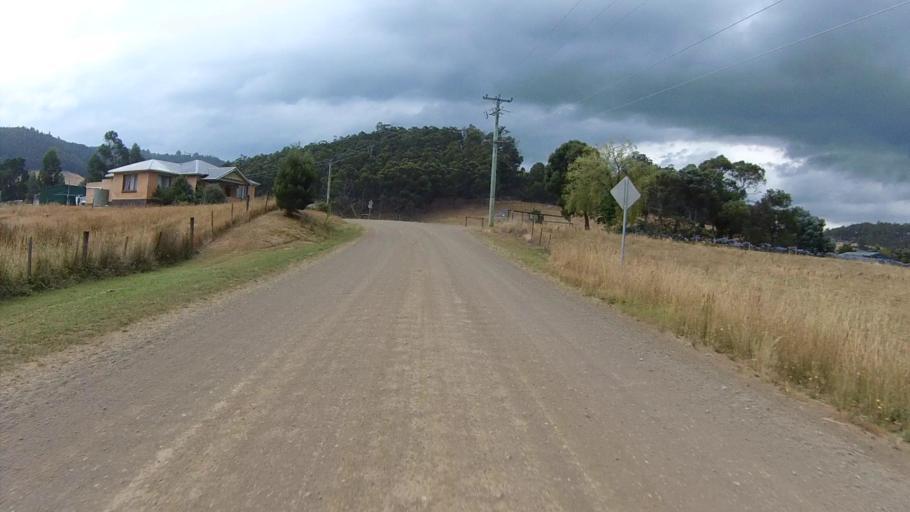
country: AU
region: Tasmania
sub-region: Huon Valley
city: Huonville
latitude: -42.9786
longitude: 147.0549
